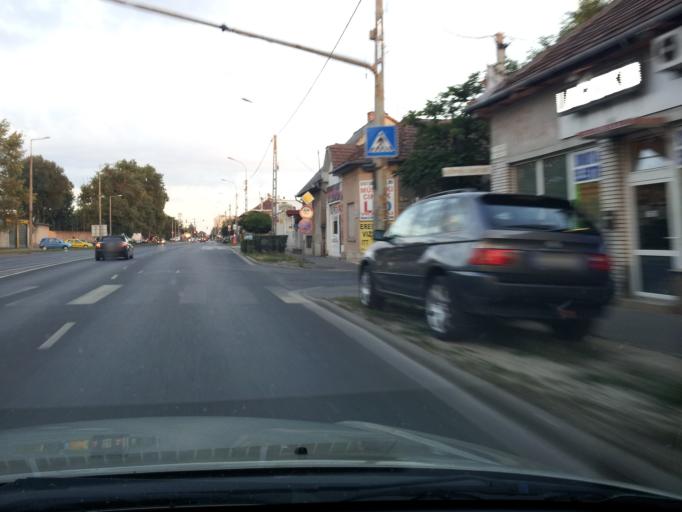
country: HU
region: Budapest
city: Budapest XV. keruelet
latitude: 47.5540
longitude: 19.1313
